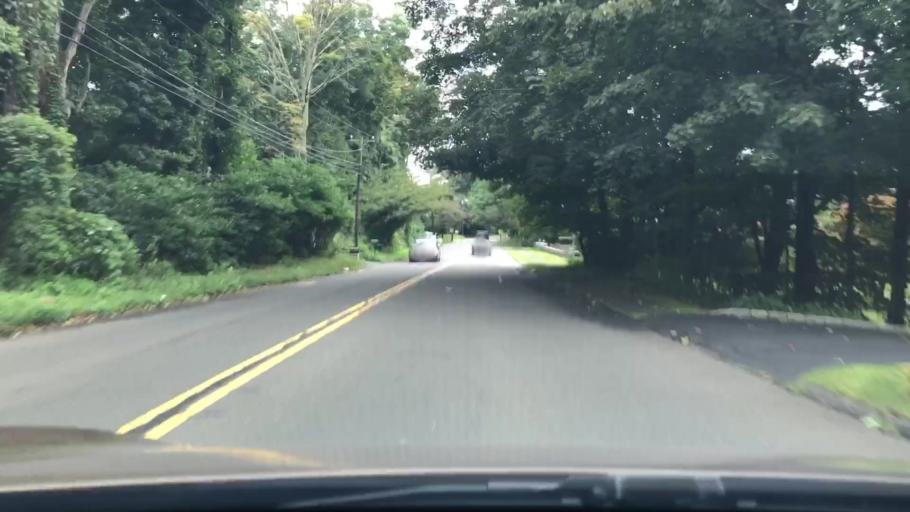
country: US
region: Connecticut
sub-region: Fairfield County
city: Norwalk
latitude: 41.1247
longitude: -73.4521
